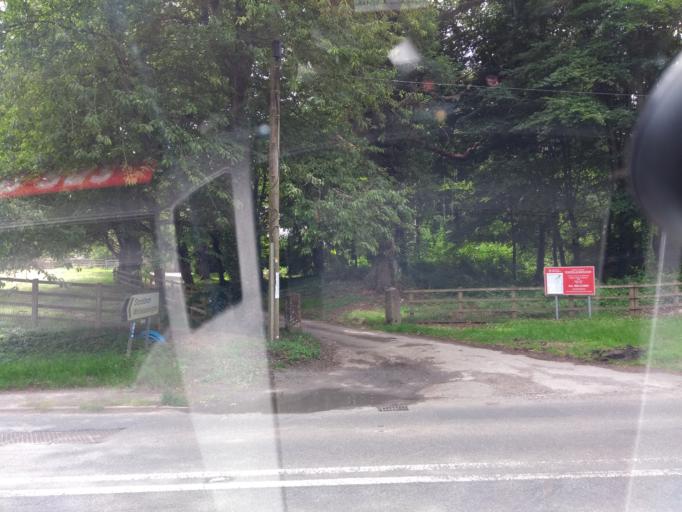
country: GB
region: England
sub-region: Somerset
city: Ilminster
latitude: 50.9345
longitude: -2.8849
